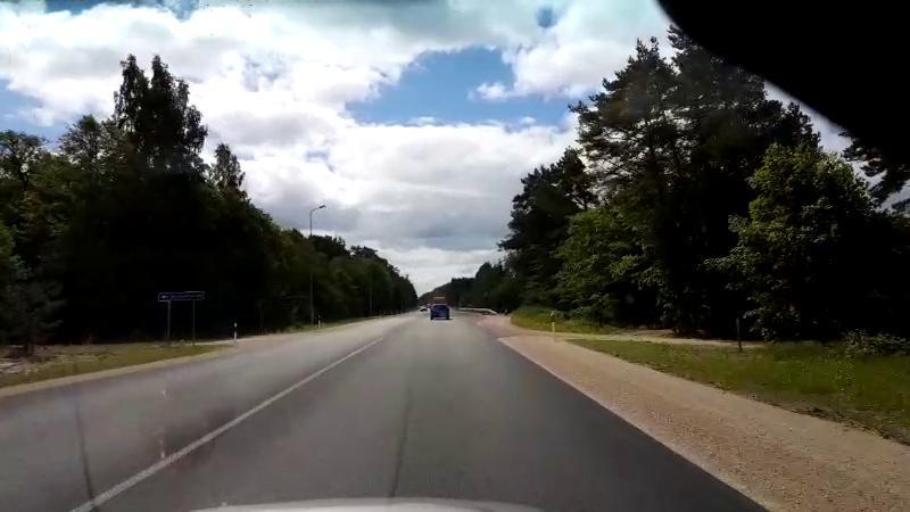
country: LV
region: Salacgrivas
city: Salacgriva
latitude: 57.7810
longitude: 24.3547
